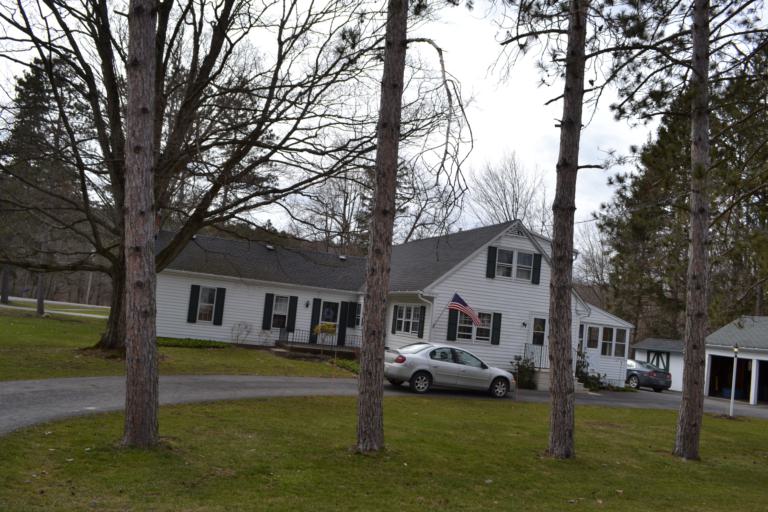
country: US
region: New York
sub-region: Erie County
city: East Aurora
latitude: 42.7090
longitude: -78.5823
